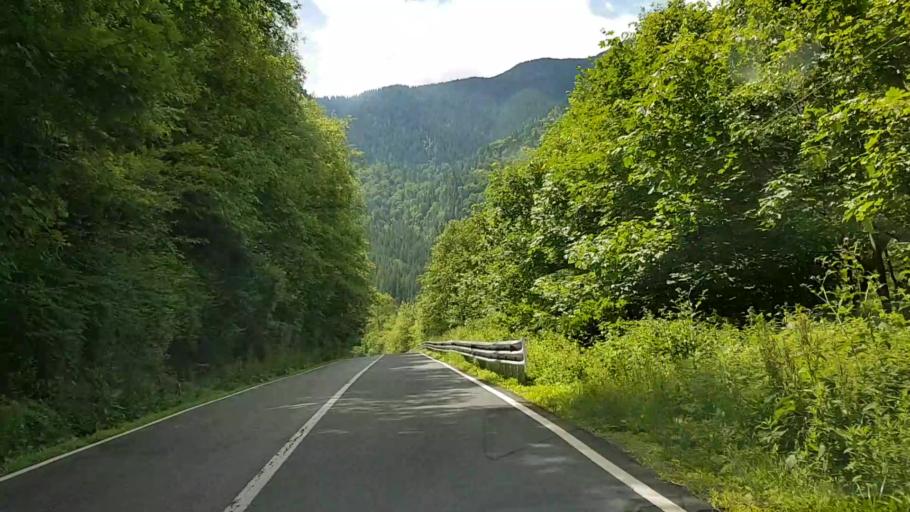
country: RO
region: Suceava
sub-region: Comuna Crucea
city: Crucea
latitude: 47.3858
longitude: 25.5795
